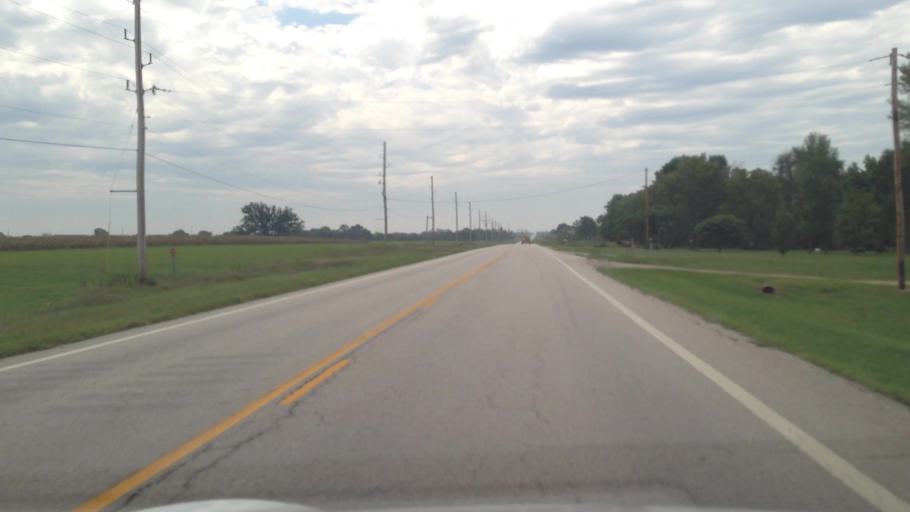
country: US
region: Kansas
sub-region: Allen County
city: Iola
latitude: 37.9576
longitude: -95.1701
